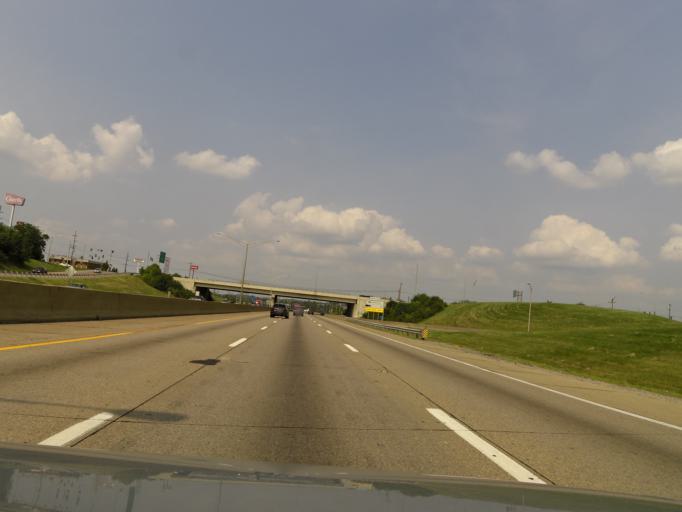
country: US
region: Kentucky
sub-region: Kenton County
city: Crescent Springs
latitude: 39.0456
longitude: -84.5765
